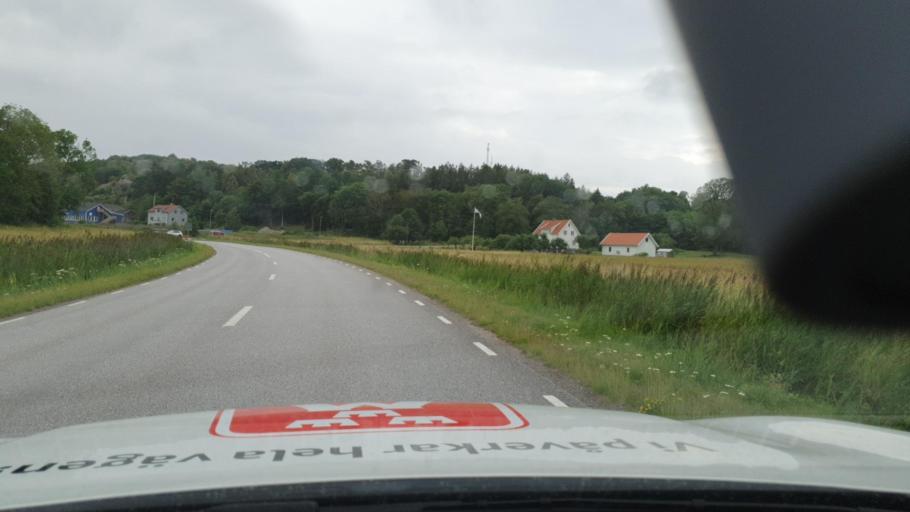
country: SE
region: Vaestra Goetaland
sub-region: Sotenas Kommun
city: Hunnebostrand
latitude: 58.4552
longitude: 11.3165
